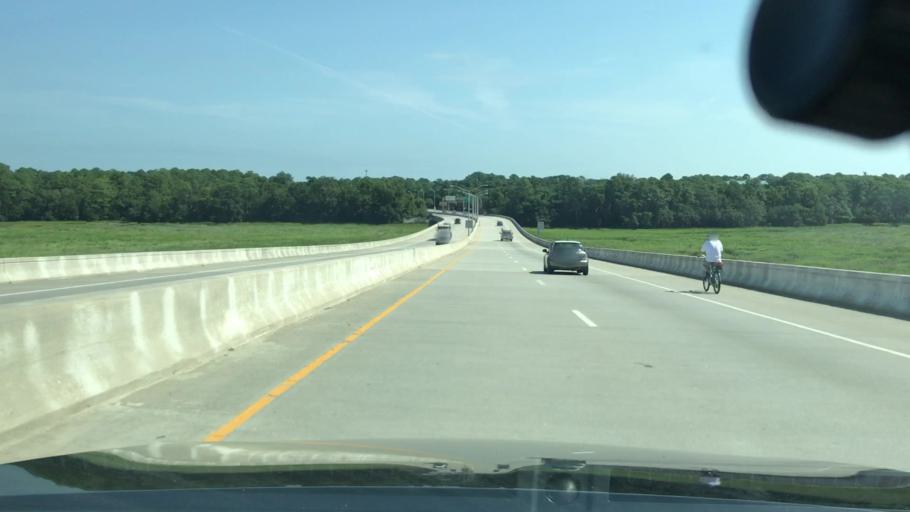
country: US
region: South Carolina
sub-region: Beaufort County
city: Hilton Head Island
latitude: 32.1804
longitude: -80.7676
